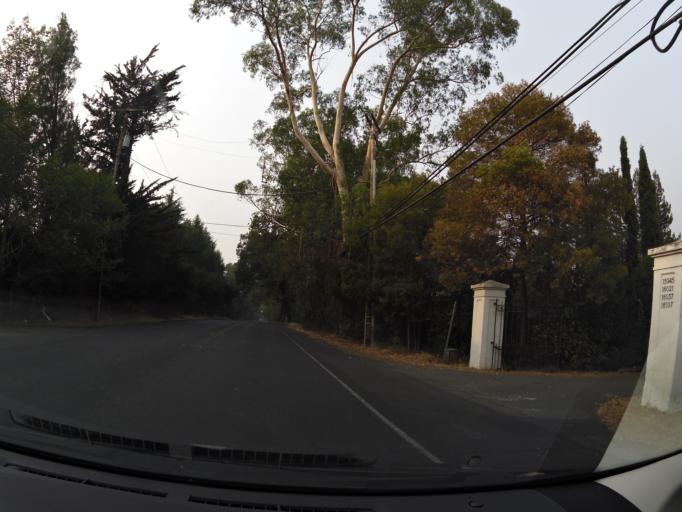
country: US
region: California
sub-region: Sonoma County
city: Eldridge
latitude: 38.3297
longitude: -122.5085
